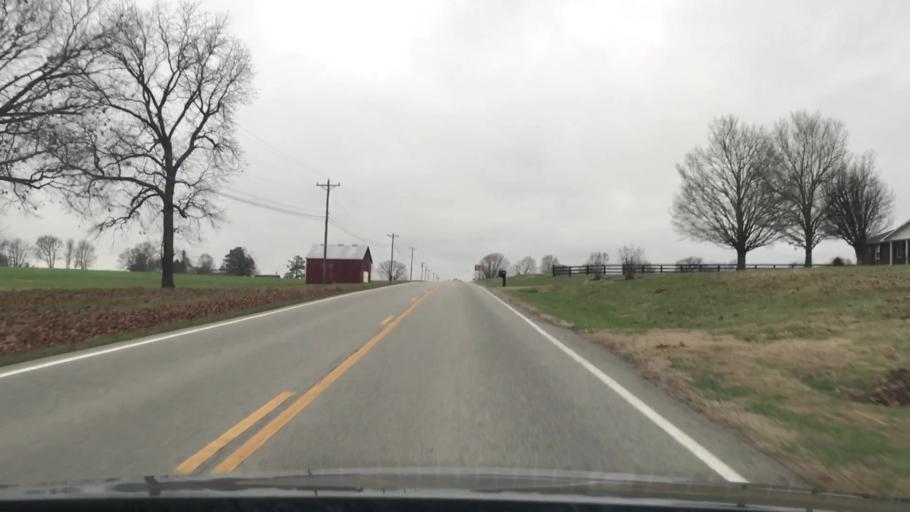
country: US
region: Kentucky
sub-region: Todd County
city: Elkton
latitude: 36.7622
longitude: -87.1672
